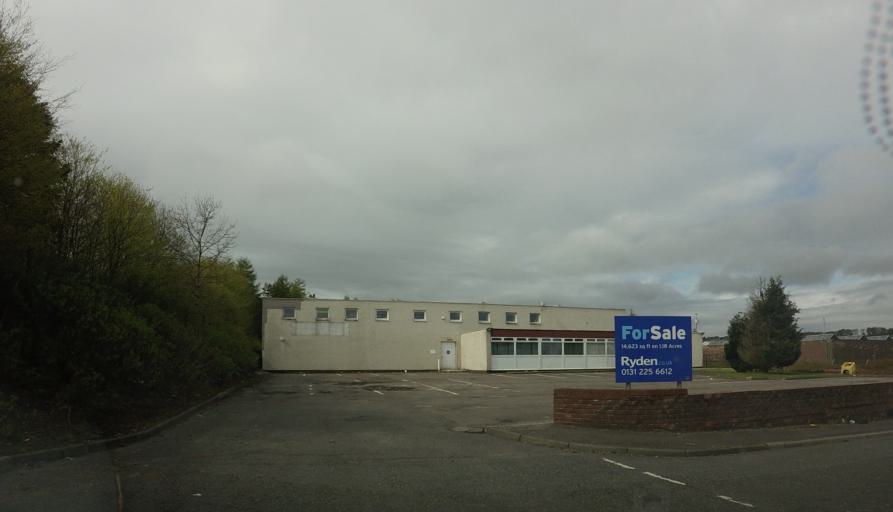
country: GB
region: Scotland
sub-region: West Lothian
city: Livingston
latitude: 55.9092
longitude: -3.5710
